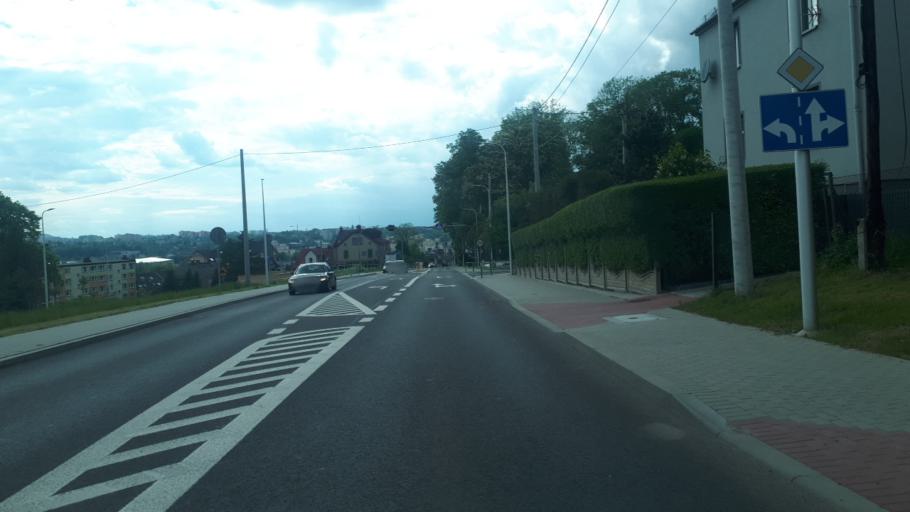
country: PL
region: Silesian Voivodeship
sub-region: Bielsko-Biala
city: Bielsko-Biala
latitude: 49.8206
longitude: 19.0685
